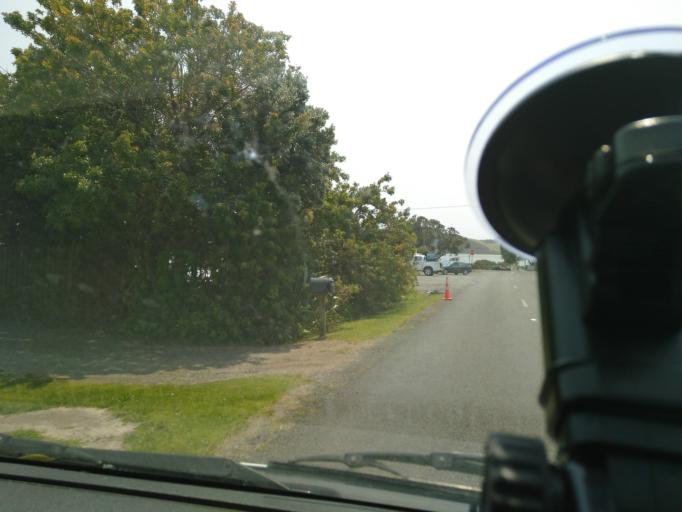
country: NZ
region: Northland
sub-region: Far North District
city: Kaitaia
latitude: -34.8154
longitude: 173.1173
